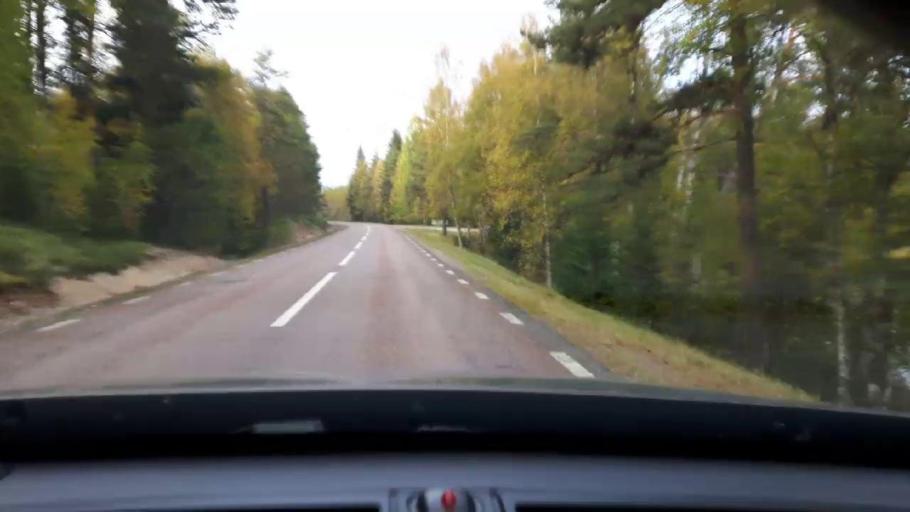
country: SE
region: Dalarna
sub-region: Gagnefs Kommun
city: Mockfjard
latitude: 60.3332
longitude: 14.9230
